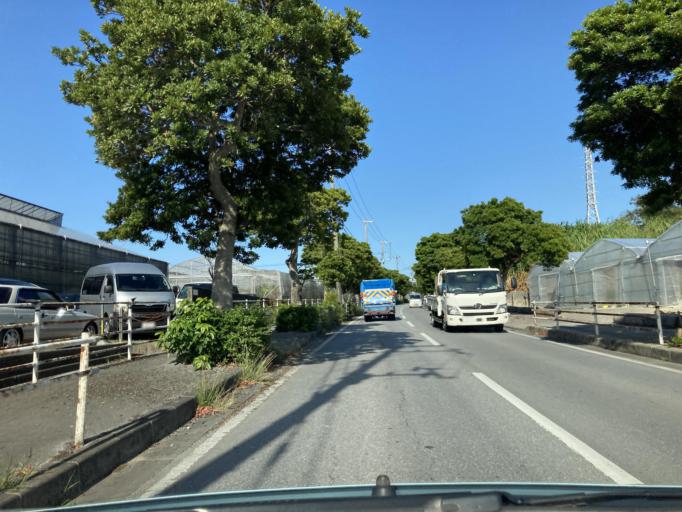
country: JP
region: Okinawa
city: Tomigusuku
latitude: 26.1719
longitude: 127.7034
